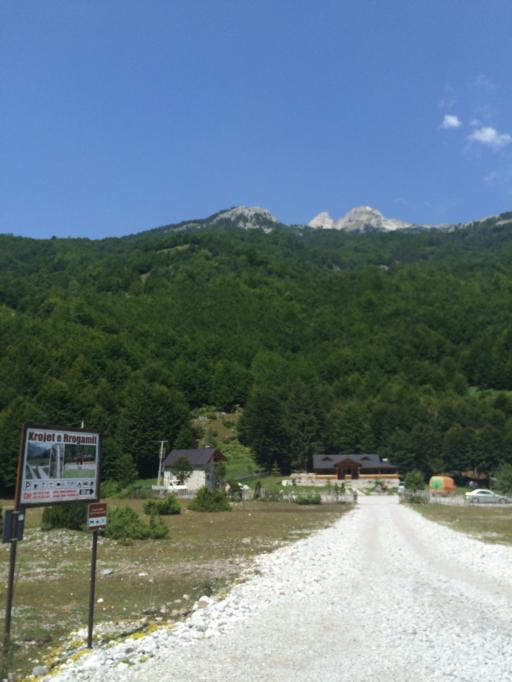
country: AL
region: Kukes
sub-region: Rrethi i Tropojes
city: Valbone
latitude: 42.4302
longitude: 19.8732
